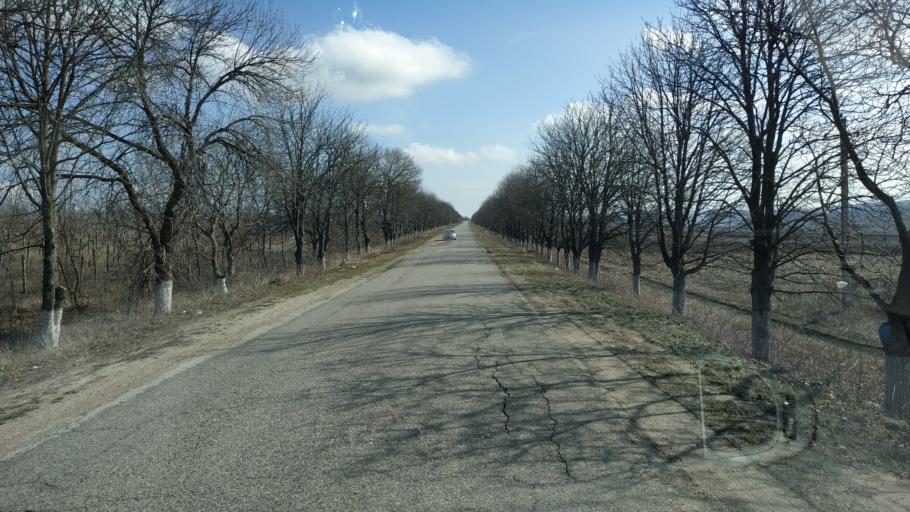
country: MD
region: Hincesti
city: Hincesti
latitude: 46.8563
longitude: 28.6379
